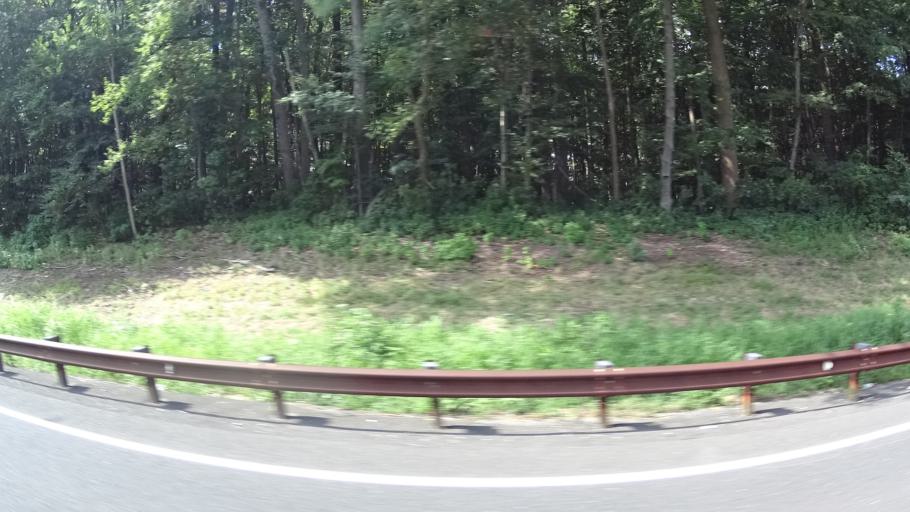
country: US
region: New Jersey
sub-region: Monmouth County
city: Strathmore
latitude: 40.4001
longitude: -74.1902
